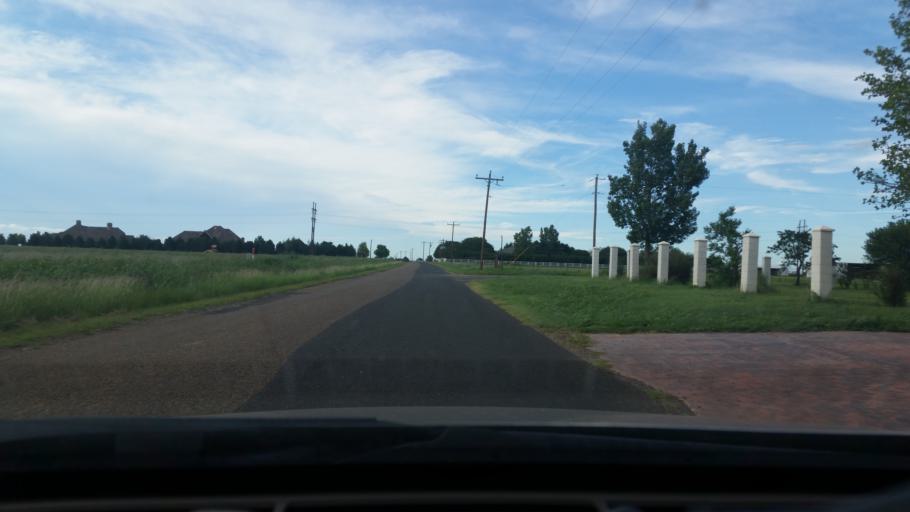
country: US
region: New Mexico
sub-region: Curry County
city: Clovis
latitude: 34.4535
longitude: -103.1784
